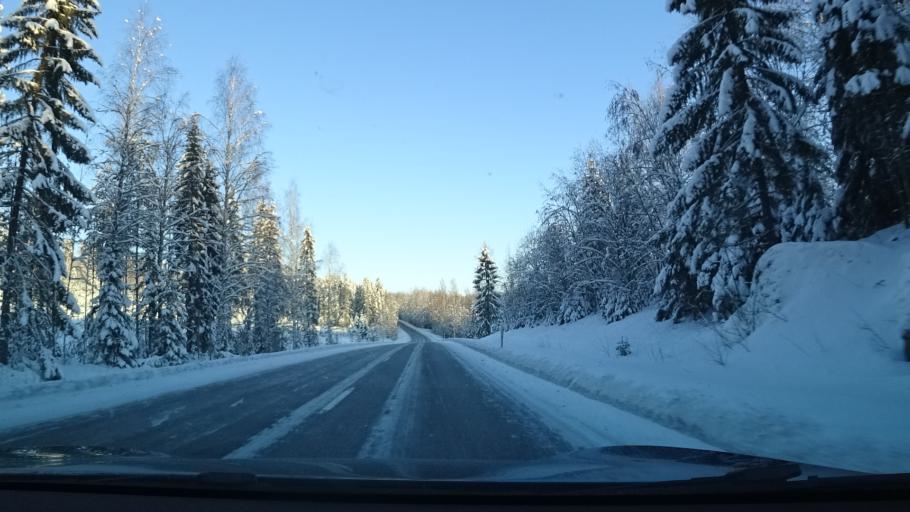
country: FI
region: Southern Savonia
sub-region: Savonlinna
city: Heinaevesi
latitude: 62.5259
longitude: 28.4749
